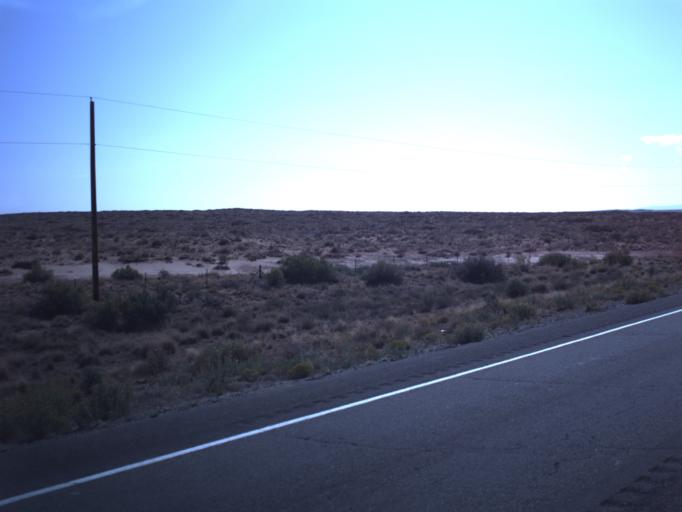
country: US
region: Utah
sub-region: San Juan County
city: Blanding
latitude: 37.1325
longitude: -109.5522
